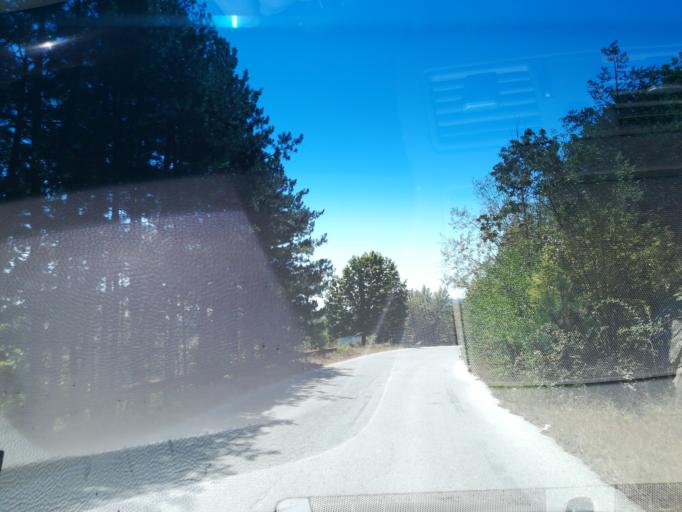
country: BG
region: Pazardzhik
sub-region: Obshtina Strelcha
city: Strelcha
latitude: 42.5492
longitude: 24.3370
